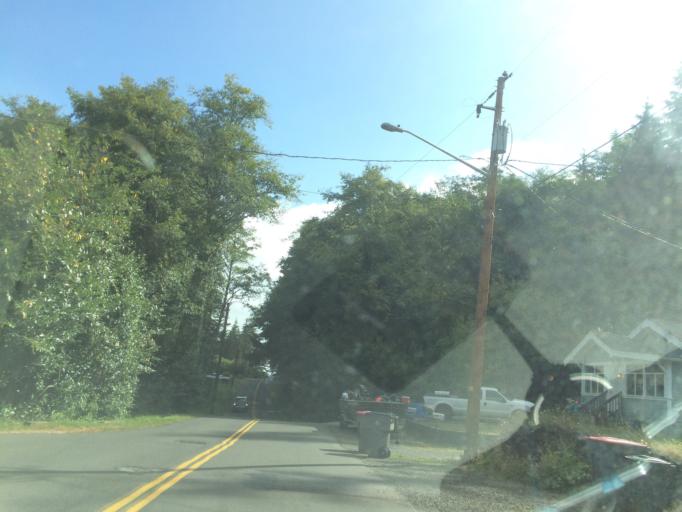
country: US
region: Oregon
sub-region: Clatsop County
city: Astoria
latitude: 46.1860
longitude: -123.8128
